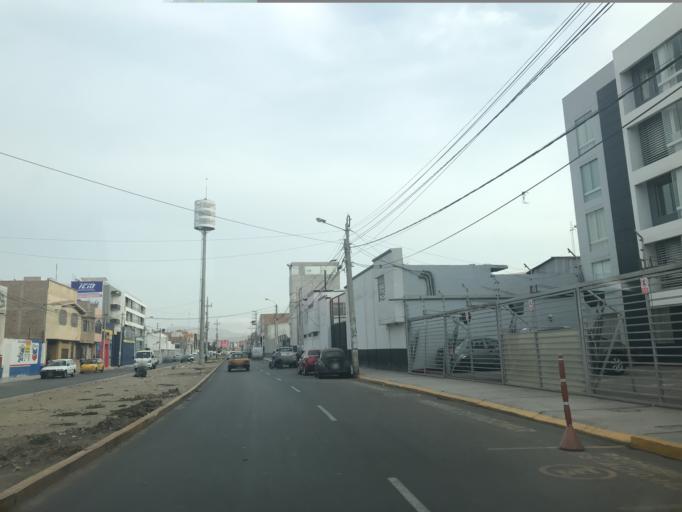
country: PE
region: Lambayeque
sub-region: Provincia de Chiclayo
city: Chiclayo
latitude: -6.7887
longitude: -79.8440
